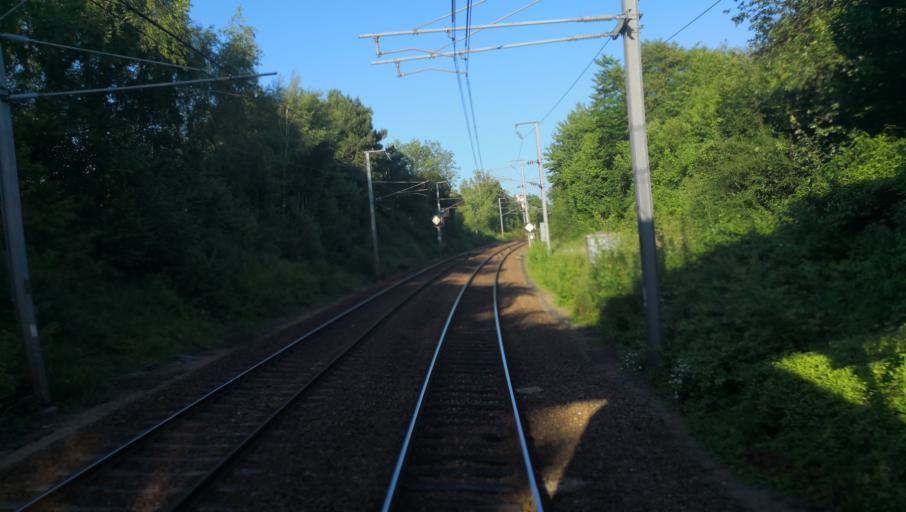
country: FR
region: Haute-Normandie
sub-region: Departement de l'Eure
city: Serquigny
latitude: 49.1085
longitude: 0.7249
